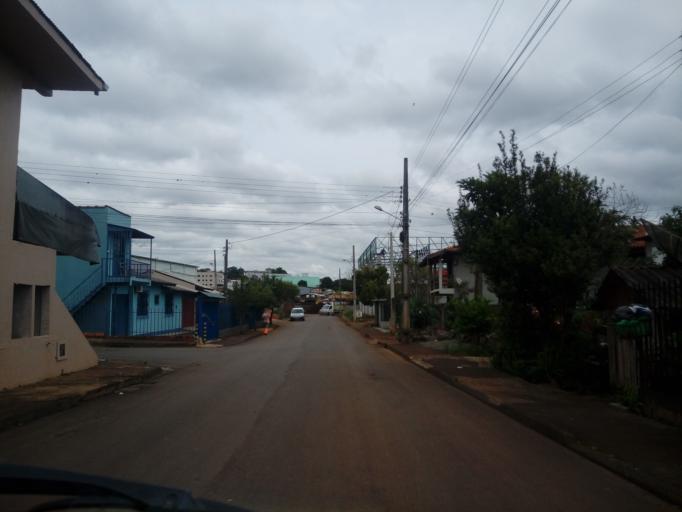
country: BR
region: Santa Catarina
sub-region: Chapeco
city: Chapeco
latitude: -27.0705
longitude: -52.6201
